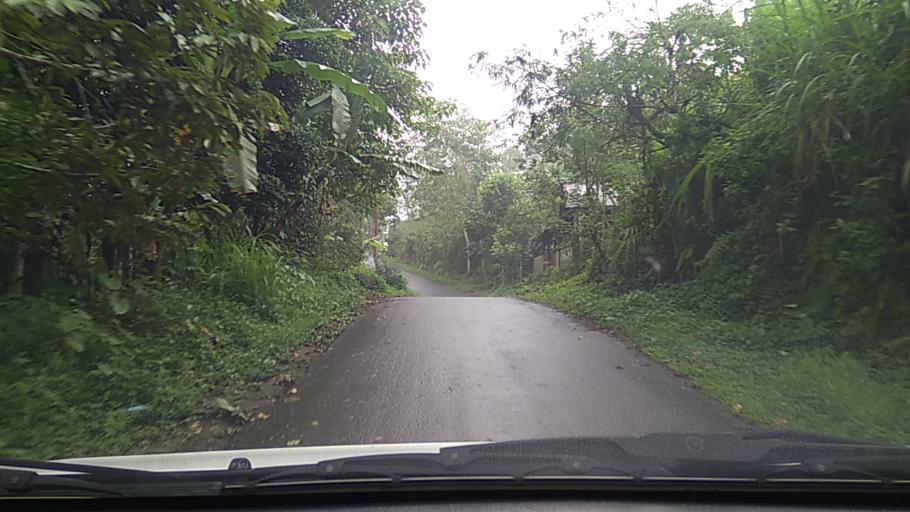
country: ID
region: Bali
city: Banjar Ambengan
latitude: -8.1980
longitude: 115.1793
